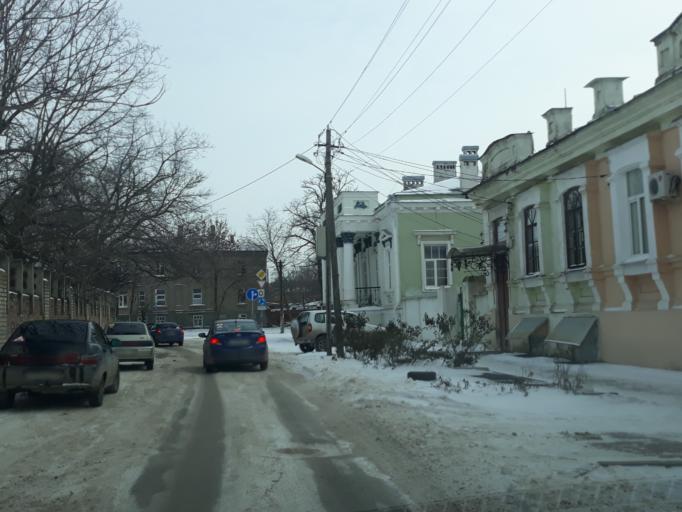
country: RU
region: Rostov
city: Taganrog
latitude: 47.2102
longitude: 38.9196
